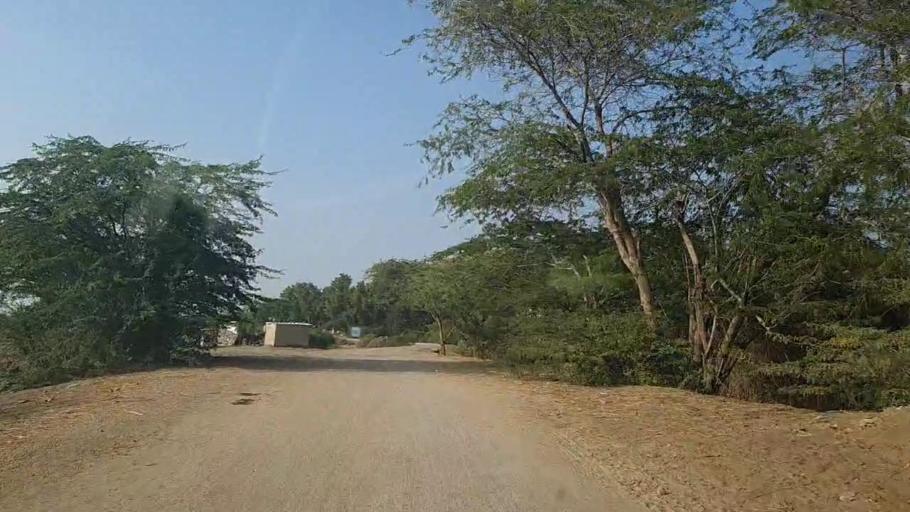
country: PK
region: Sindh
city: Mirpur Sakro
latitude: 24.5725
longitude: 67.6661
